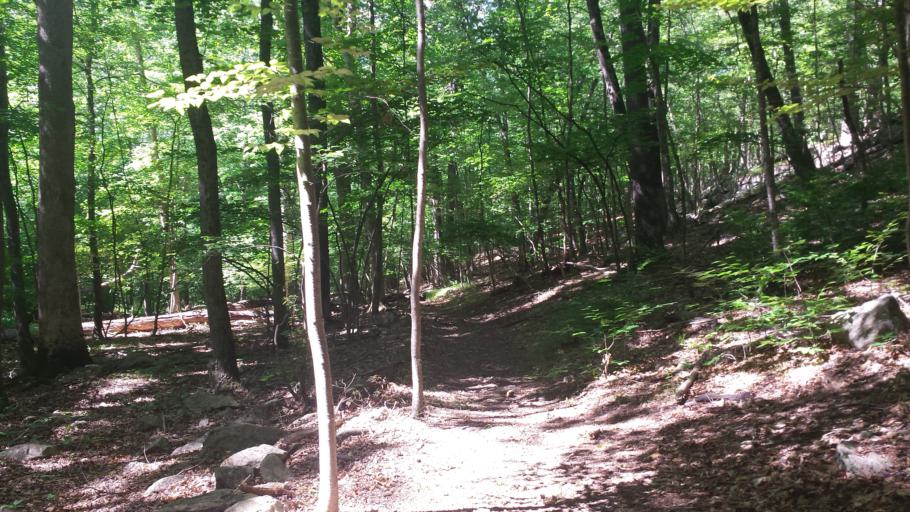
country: US
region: New York
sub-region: Westchester County
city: Pound Ridge
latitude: 41.2569
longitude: -73.5802
